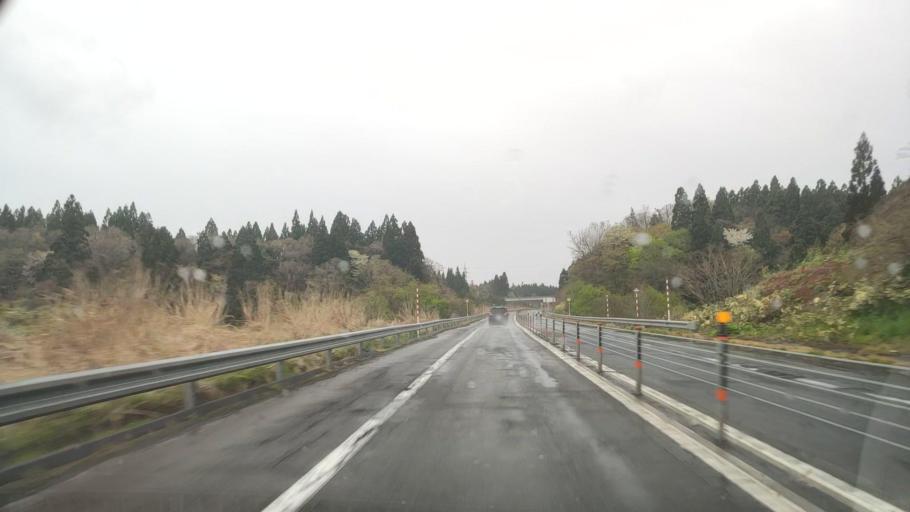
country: JP
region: Akita
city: Noshiromachi
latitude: 40.1706
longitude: 140.0527
